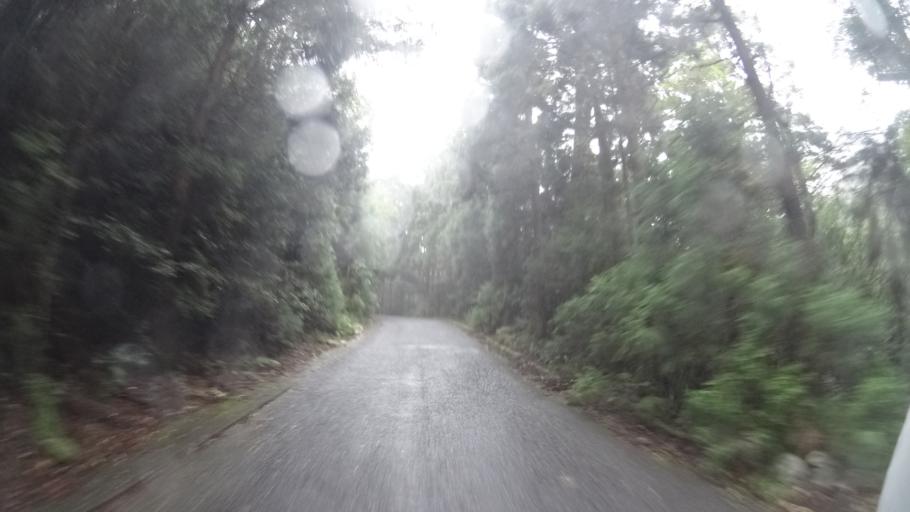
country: JP
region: Kagoshima
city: Nishinoomote
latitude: 30.3039
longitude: 130.5760
